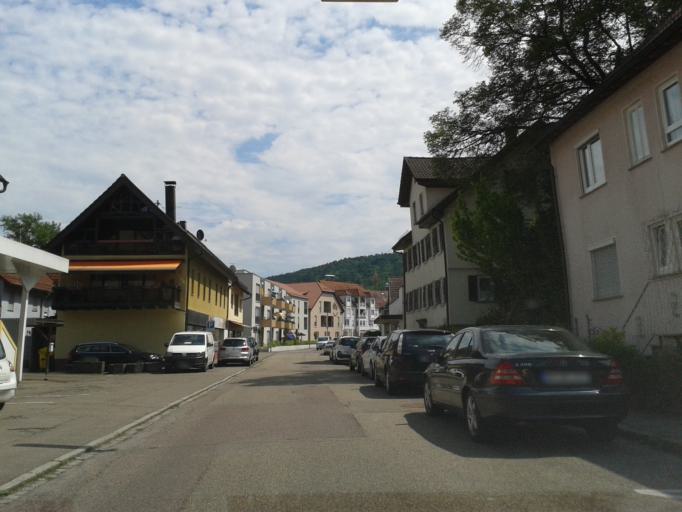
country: DE
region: Baden-Wuerttemberg
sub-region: Regierungsbezirk Stuttgart
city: Murrhardt
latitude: 48.9816
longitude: 9.5769
